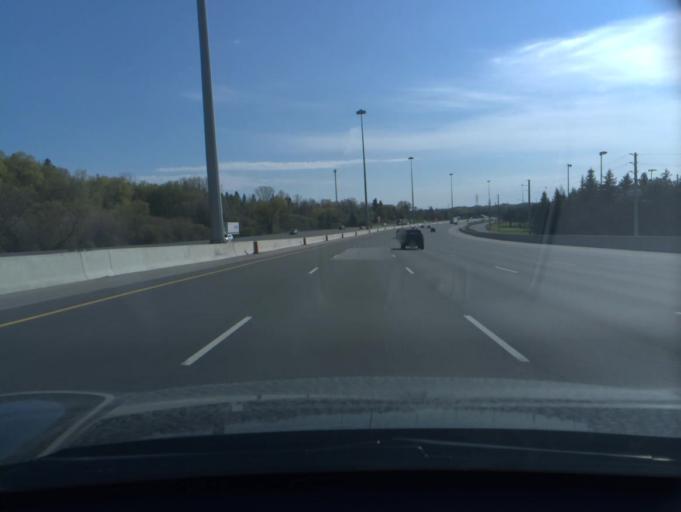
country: CA
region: Ontario
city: North Perth
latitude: 43.8232
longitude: -81.0002
